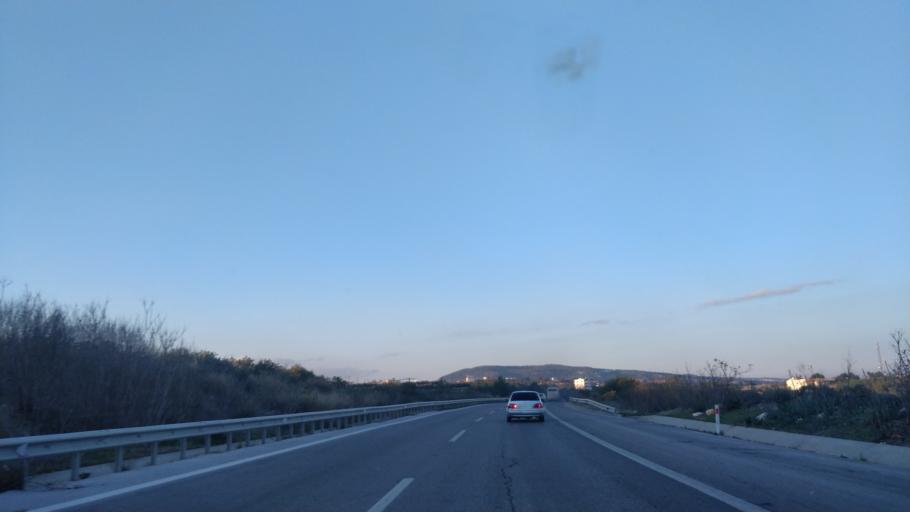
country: TR
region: Mersin
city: Elvanli
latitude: 36.7158
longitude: 34.4273
